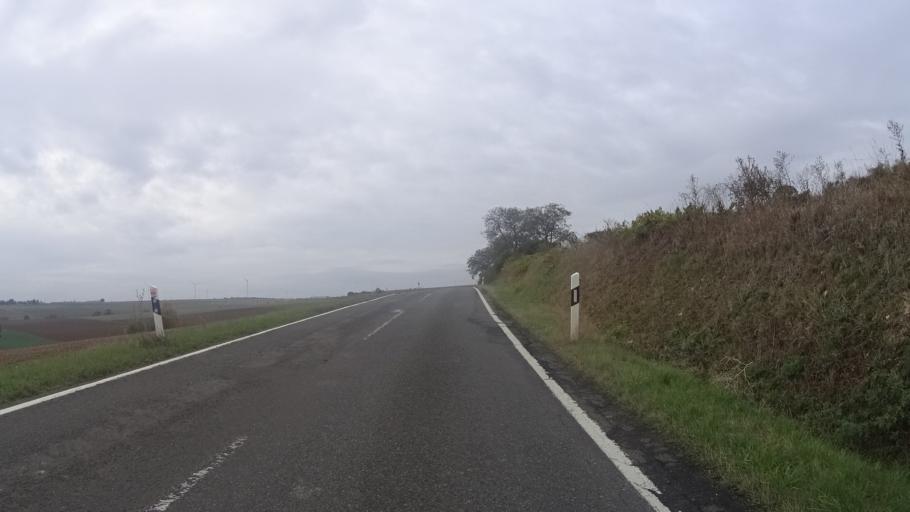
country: DE
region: Rheinland-Pfalz
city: Ottersheim
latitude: 49.6198
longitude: 8.1024
